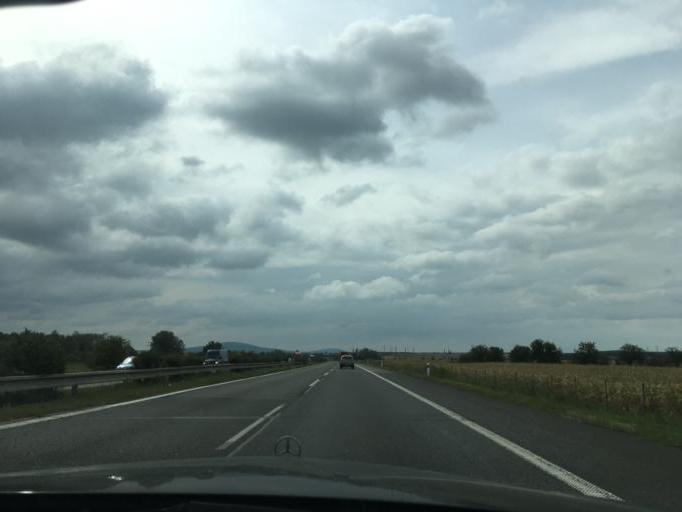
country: SK
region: Bratislavsky
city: Stupava
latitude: 48.3075
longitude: 17.0169
